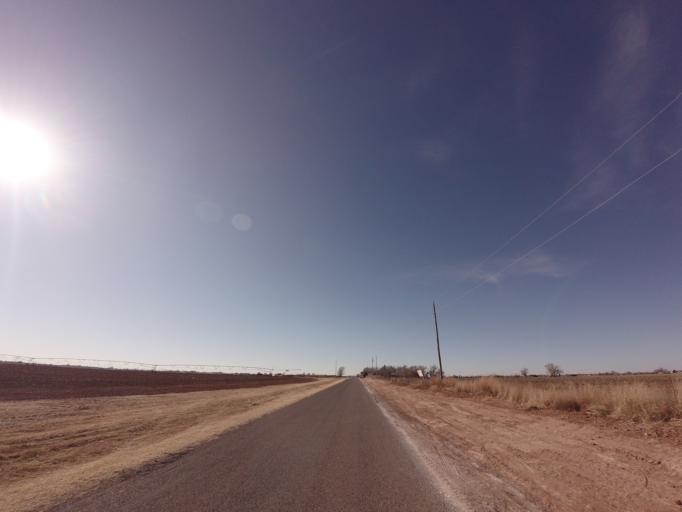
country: US
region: New Mexico
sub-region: Curry County
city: Clovis
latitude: 34.4049
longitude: -103.1473
